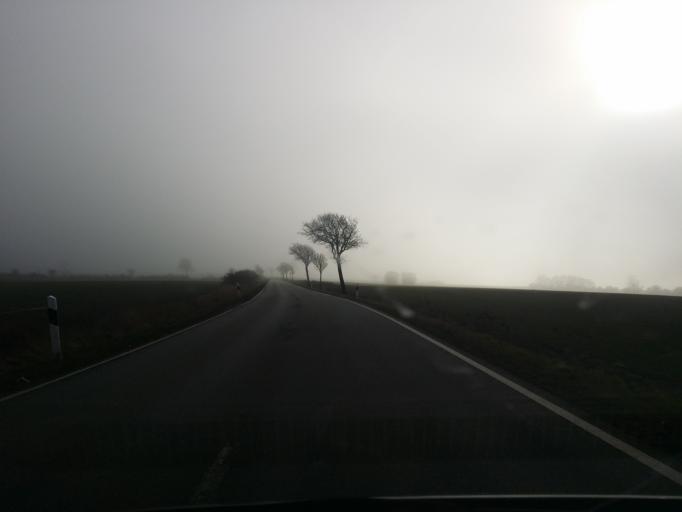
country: DE
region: Schleswig-Holstein
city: Fehmarn
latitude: 54.4419
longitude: 11.1388
